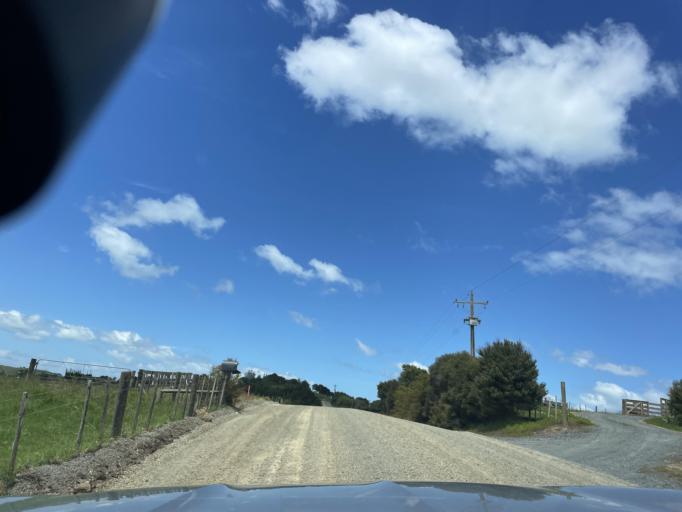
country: NZ
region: Auckland
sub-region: Auckland
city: Wellsford
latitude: -36.1581
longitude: 174.2866
